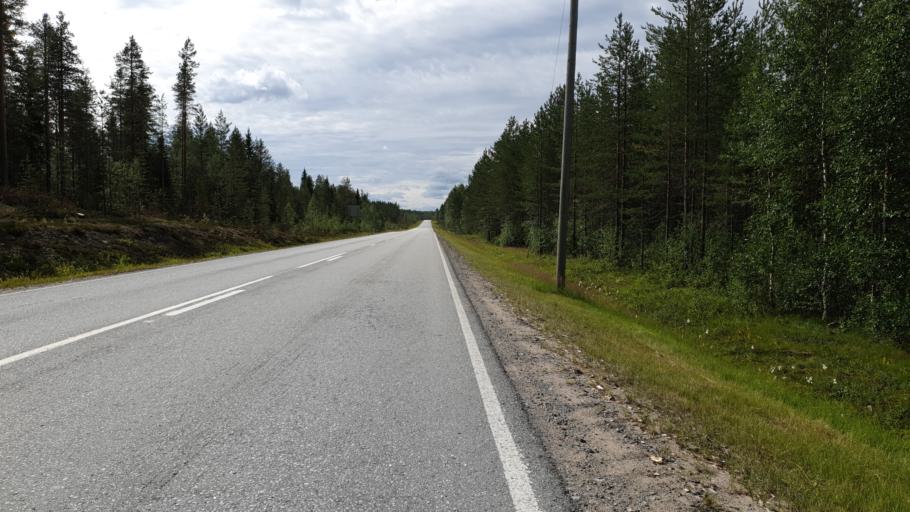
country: FI
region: Kainuu
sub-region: Kehys-Kainuu
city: Kuhmo
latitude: 64.5295
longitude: 29.9448
